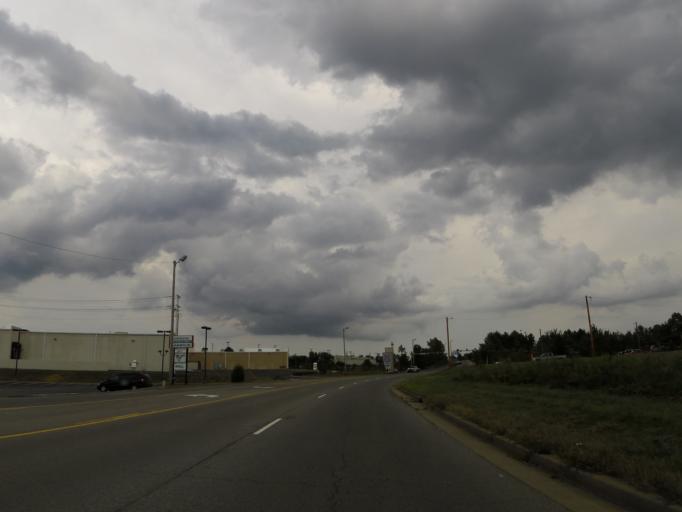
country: US
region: Tennessee
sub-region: Dickson County
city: Dickson
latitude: 36.0638
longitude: -87.3841
